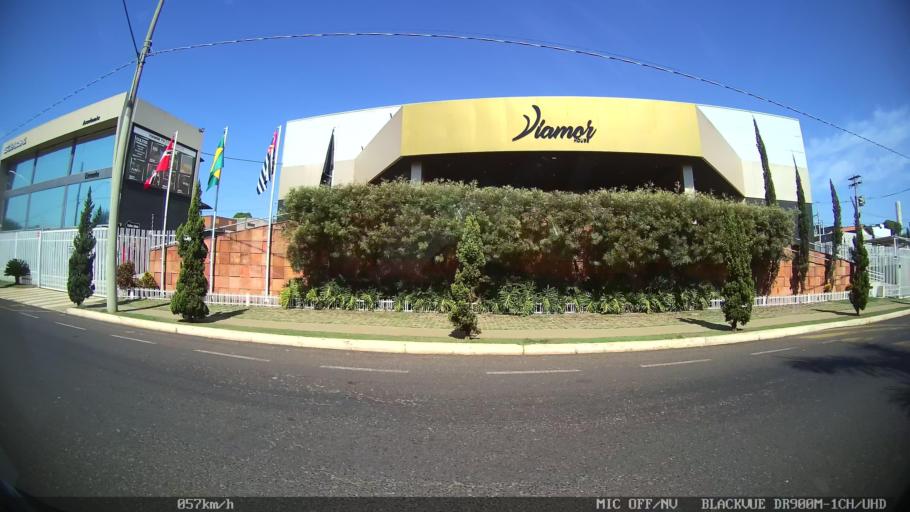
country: BR
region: Sao Paulo
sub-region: Sao Jose Do Rio Preto
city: Sao Jose do Rio Preto
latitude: -20.7783
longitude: -49.3894
